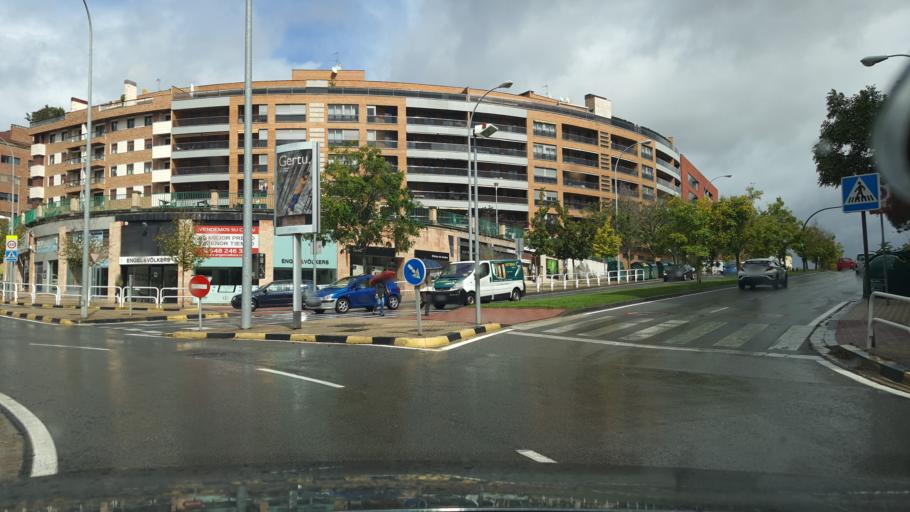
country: ES
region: Navarre
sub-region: Provincia de Navarra
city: Segundo Ensanche
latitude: 42.8066
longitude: -1.6355
